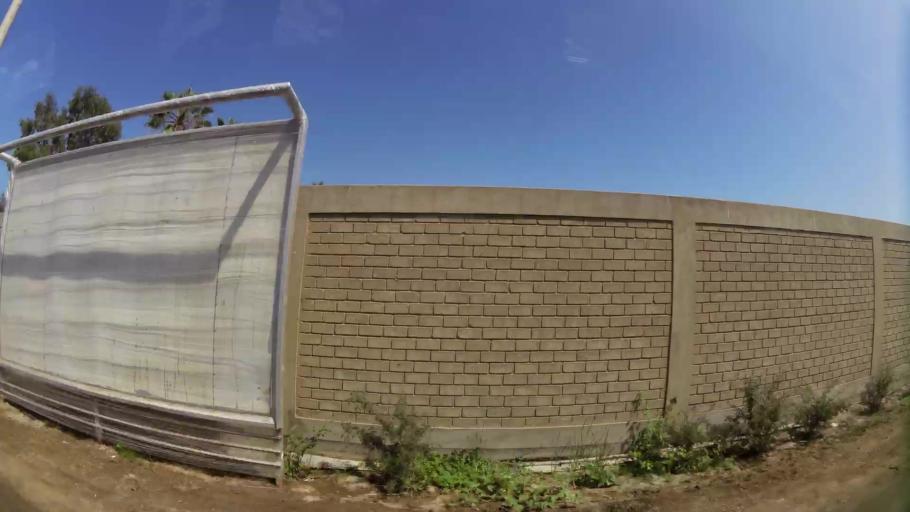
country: PE
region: Lima
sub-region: Provincia de Canete
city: Mala
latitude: -12.6834
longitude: -76.6515
